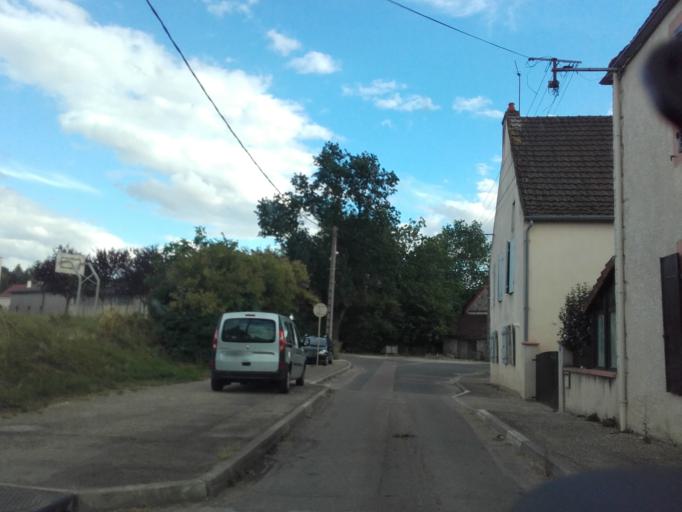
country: FR
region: Bourgogne
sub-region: Departement de Saone-et-Loire
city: Chagny
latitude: 46.9137
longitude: 4.7927
